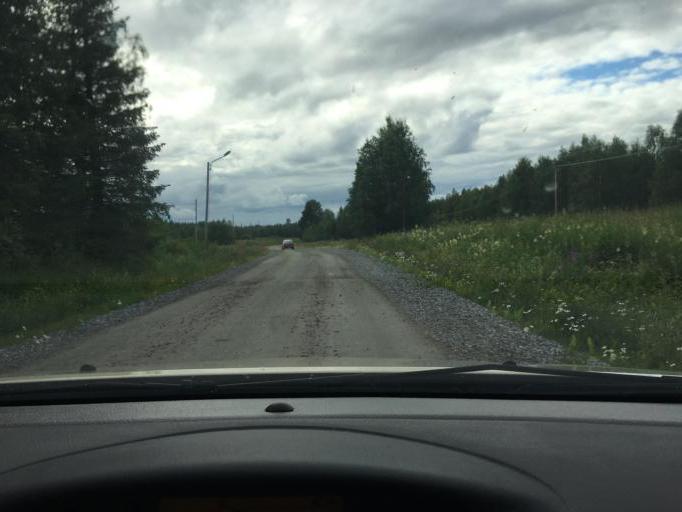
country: SE
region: Norrbotten
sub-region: Overkalix Kommun
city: OEverkalix
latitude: 66.0887
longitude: 22.8573
